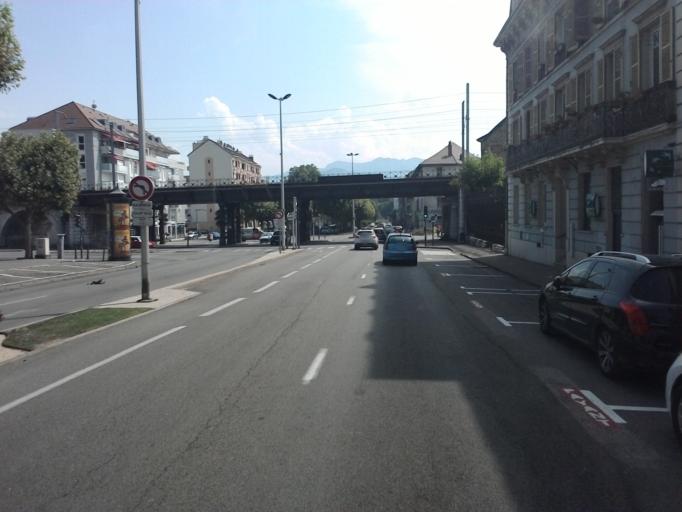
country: FR
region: Rhone-Alpes
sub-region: Departement de l'Isere
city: Voiron
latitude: 45.3657
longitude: 5.5910
